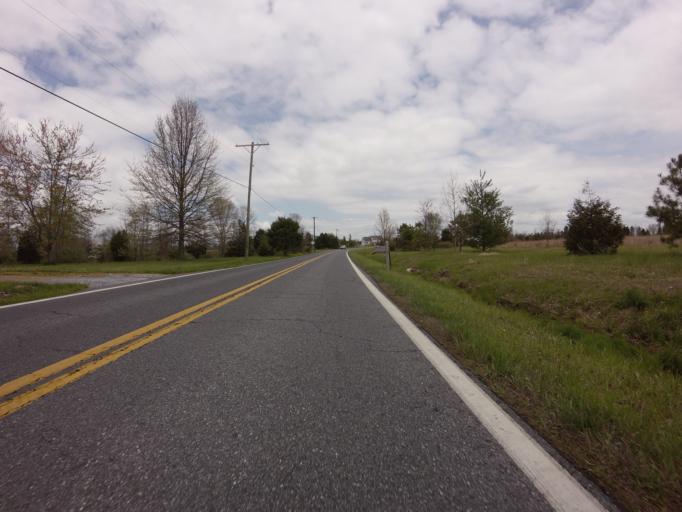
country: US
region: Maryland
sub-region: Frederick County
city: Woodsboro
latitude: 39.5692
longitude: -77.3696
